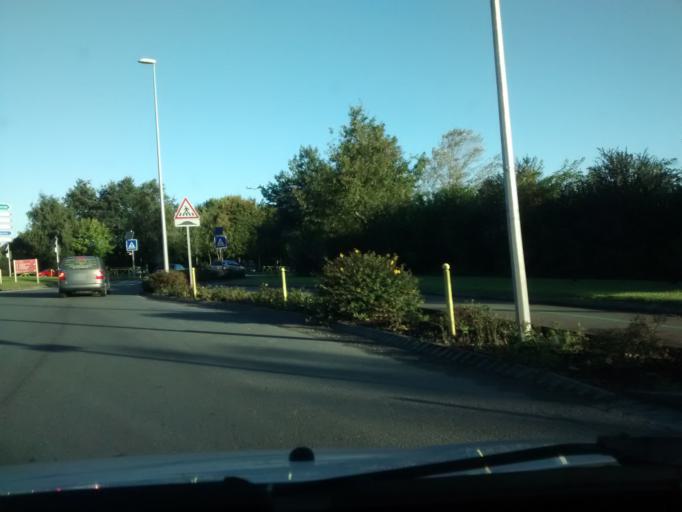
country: FR
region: Brittany
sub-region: Departement d'Ille-et-Vilaine
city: Saint-Jouan-des-Guerets
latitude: 48.6263
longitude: -1.9882
